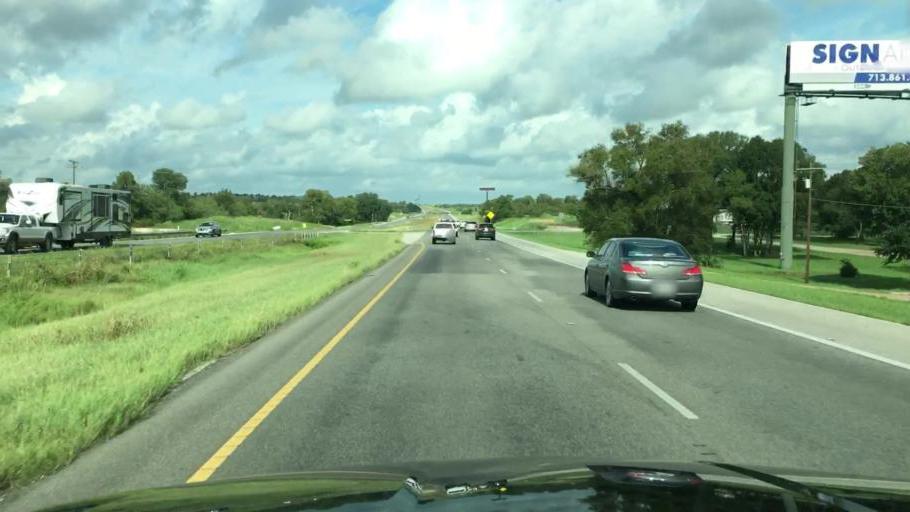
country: US
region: Texas
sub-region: Bastrop County
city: Wyldwood
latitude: 30.1615
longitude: -97.5039
